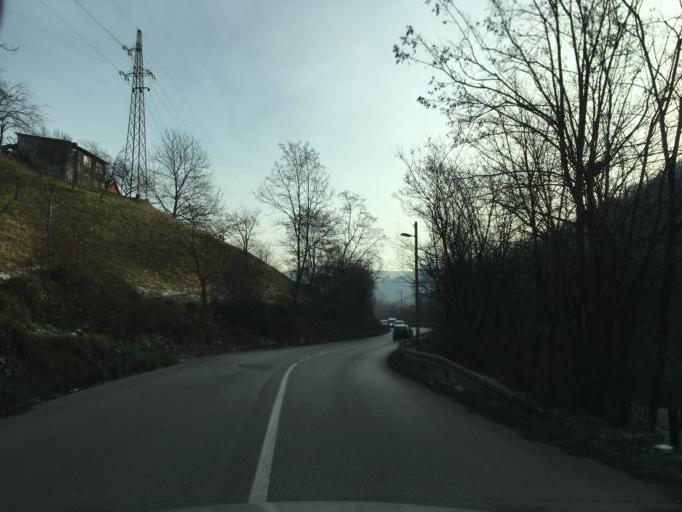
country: BA
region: Federation of Bosnia and Herzegovina
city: Lokvine
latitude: 44.1940
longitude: 17.8796
